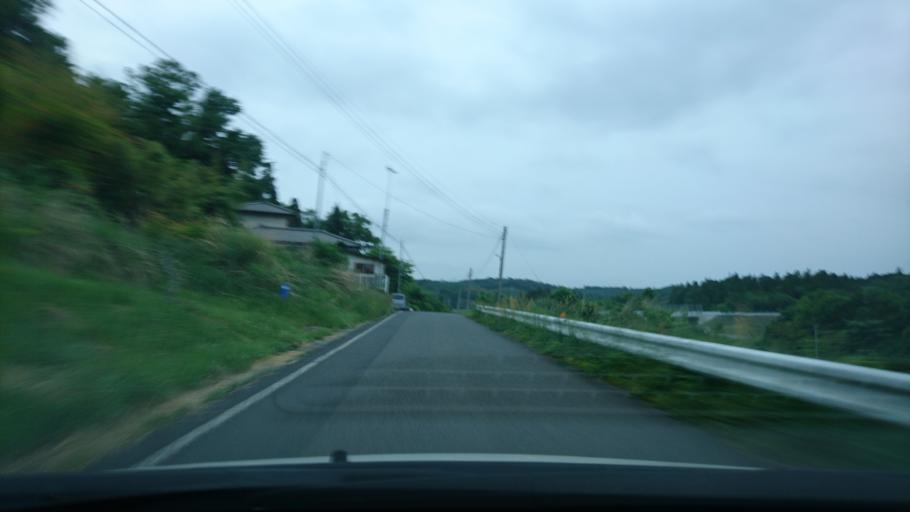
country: JP
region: Iwate
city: Ichinoseki
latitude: 38.9163
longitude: 141.1690
